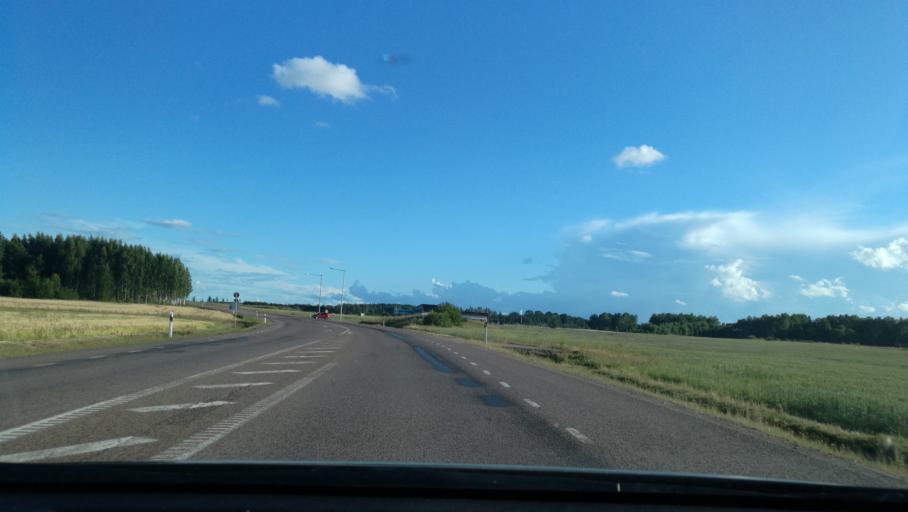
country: SE
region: Vaestmanland
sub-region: Kopings Kommun
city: Koping
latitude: 59.4855
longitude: 15.9849
